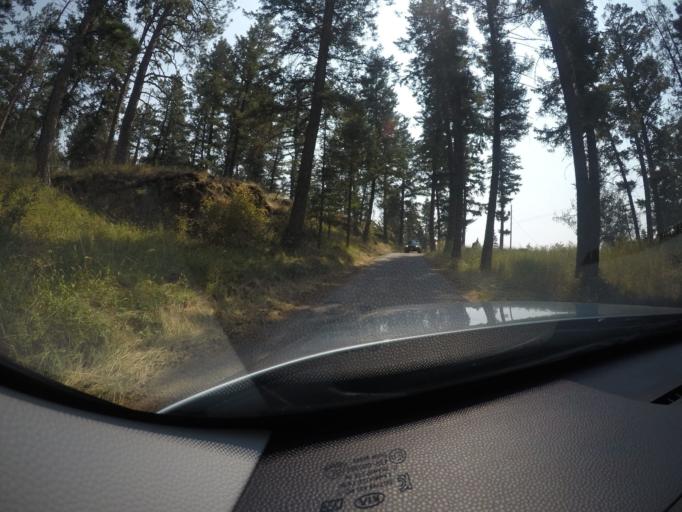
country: US
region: Montana
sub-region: Lake County
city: Polson
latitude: 47.7595
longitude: -114.1435
